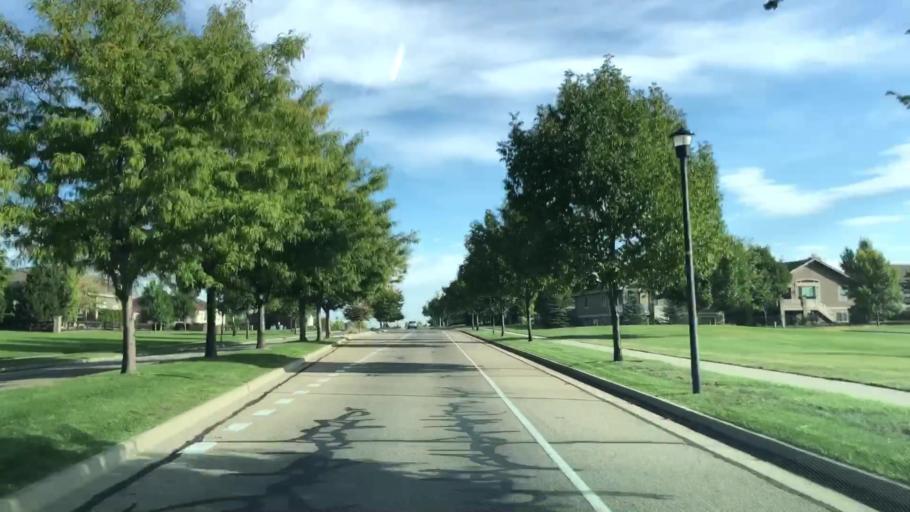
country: US
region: Colorado
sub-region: Weld County
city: Windsor
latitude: 40.4627
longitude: -104.9769
